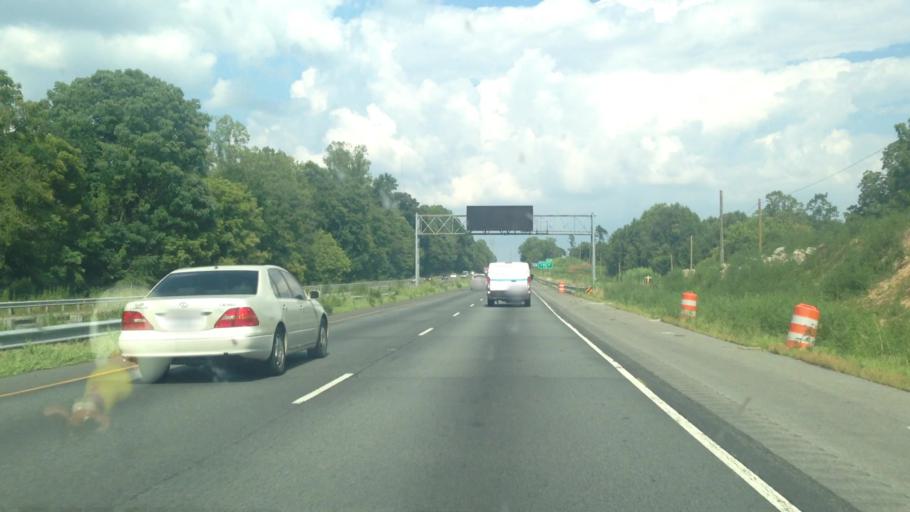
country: US
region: North Carolina
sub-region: Forsyth County
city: Kernersville
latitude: 36.1120
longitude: -80.1163
